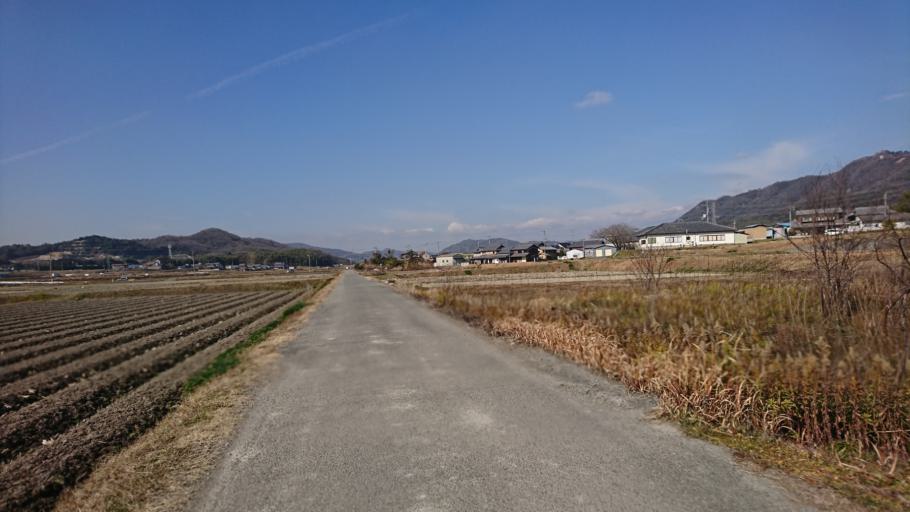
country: JP
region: Hyogo
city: Kakogawacho-honmachi
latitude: 34.8135
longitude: 134.8566
